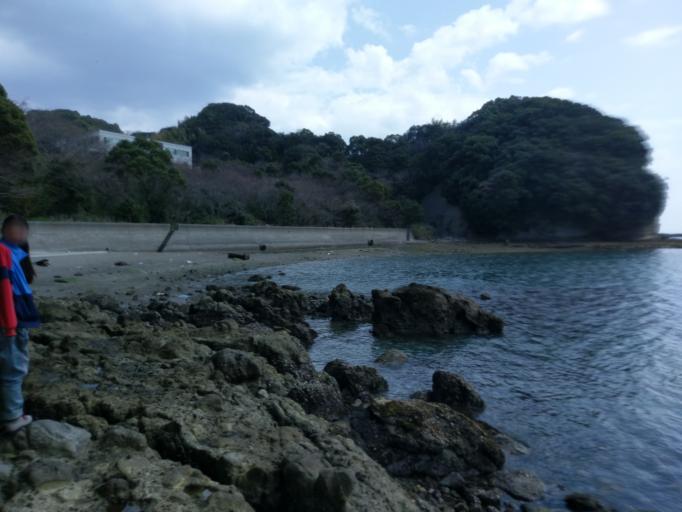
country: JP
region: Nagasaki
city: Nagasaki-shi
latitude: 32.7090
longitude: 129.9169
